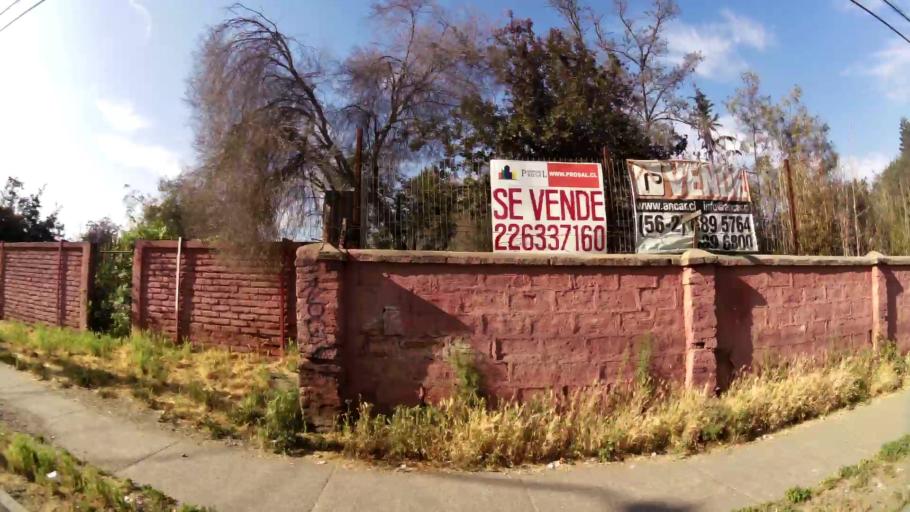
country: CL
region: Santiago Metropolitan
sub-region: Provincia de Santiago
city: La Pintana
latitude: -33.5668
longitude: -70.5908
